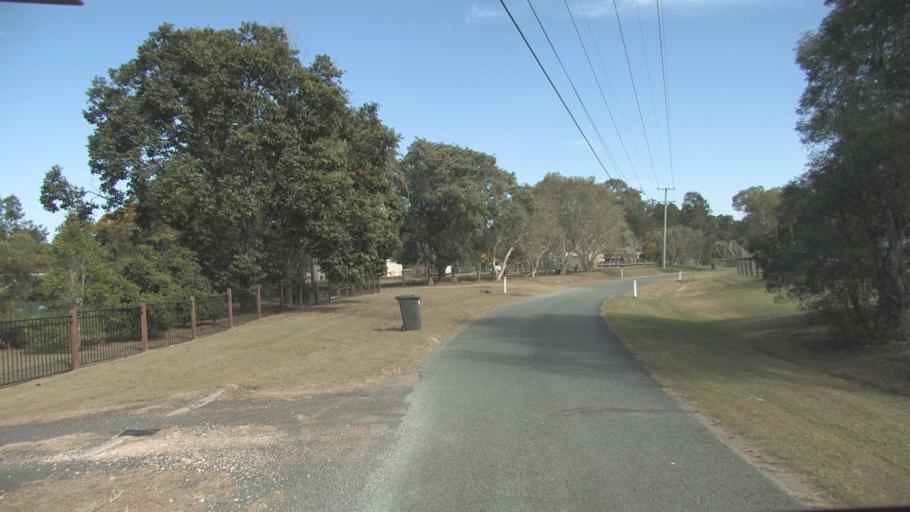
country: AU
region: Queensland
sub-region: Logan
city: North Maclean
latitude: -27.7762
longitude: 152.9952
